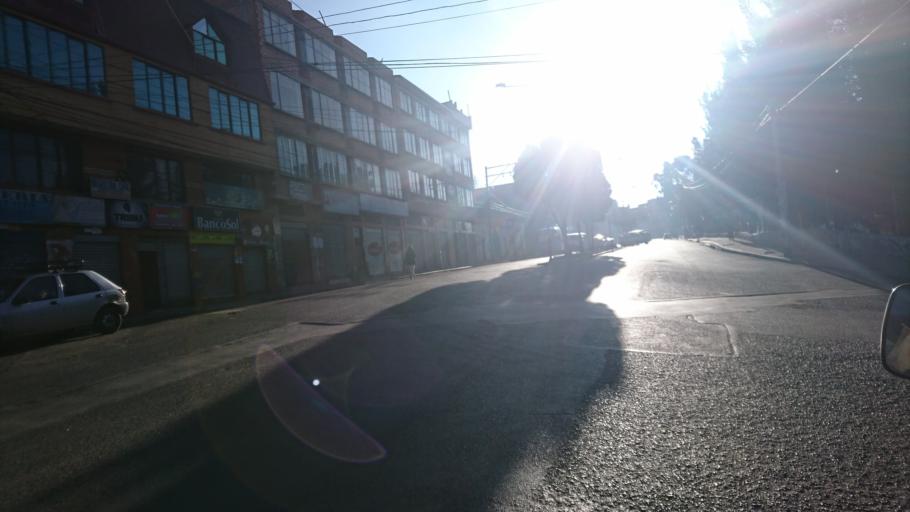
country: BO
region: La Paz
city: La Paz
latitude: -16.4959
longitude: -68.1045
